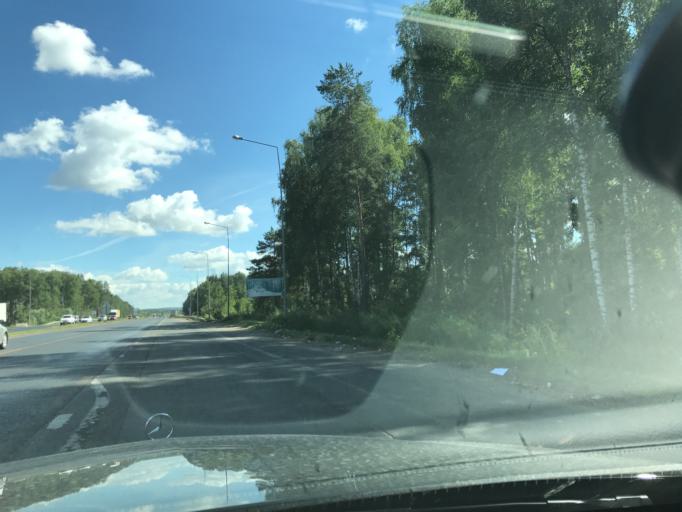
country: RU
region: Nizjnij Novgorod
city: Gorbatovka
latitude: 56.2418
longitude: 43.7251
